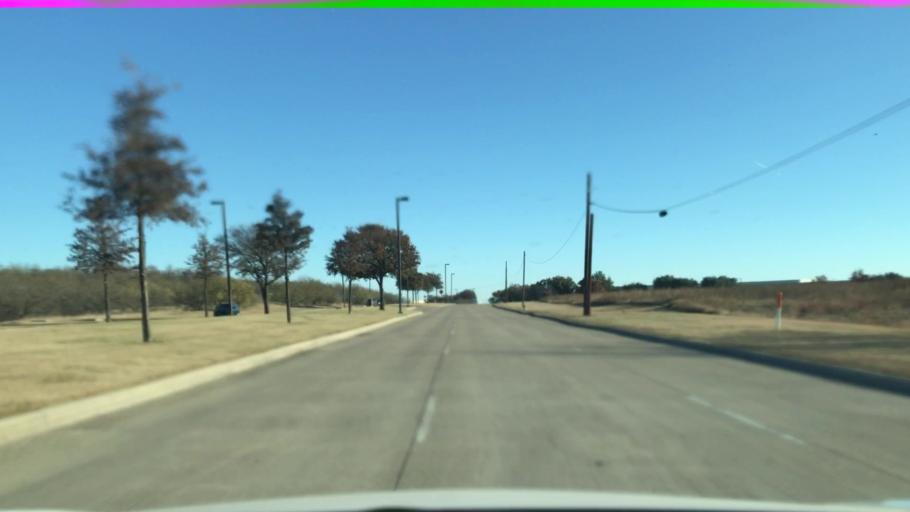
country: US
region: Texas
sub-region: Dallas County
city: Farmers Branch
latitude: 32.8862
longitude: -96.9451
